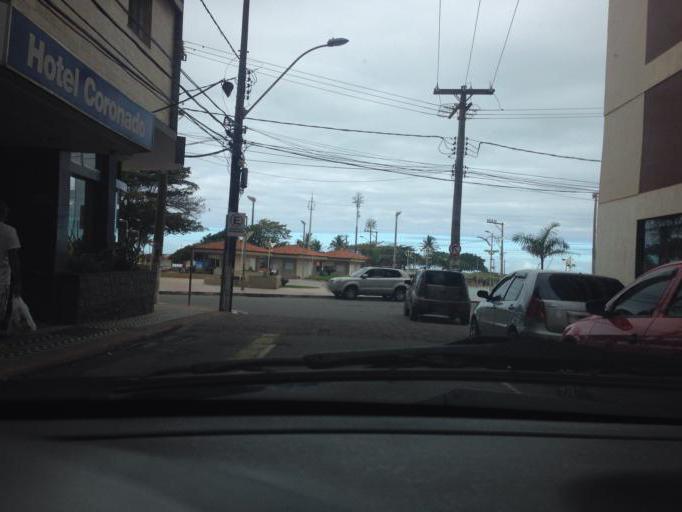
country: BR
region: Espirito Santo
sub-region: Guarapari
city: Guarapari
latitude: -20.6739
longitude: -40.4983
